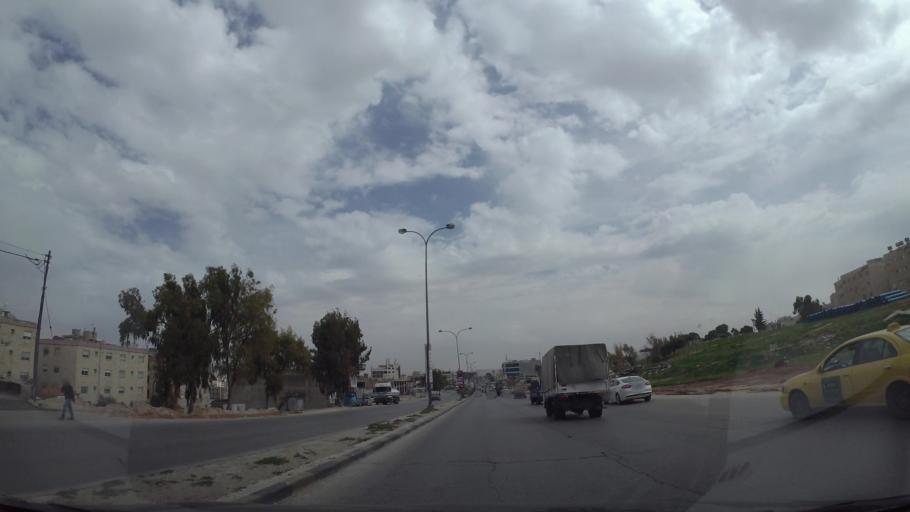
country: JO
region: Amman
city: Amman
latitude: 31.9905
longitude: 35.9408
